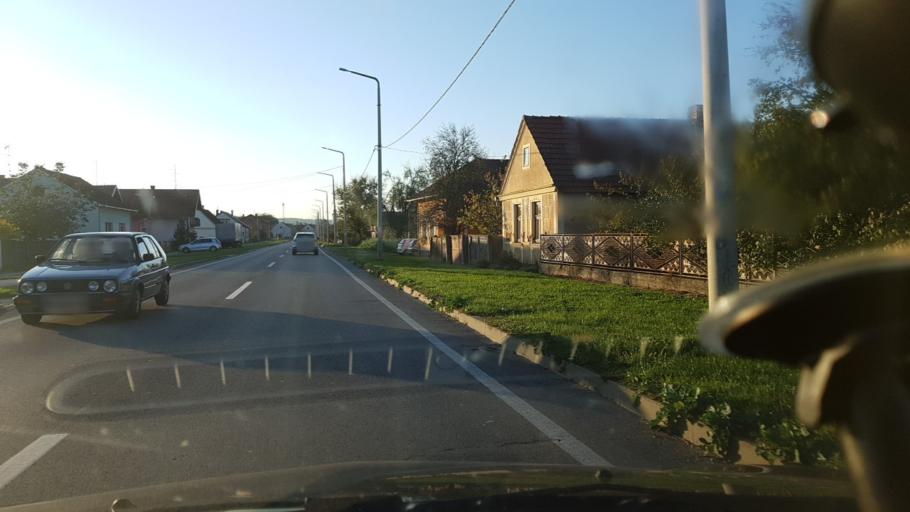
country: HR
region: Koprivnicko-Krizevacka
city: Virje
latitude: 46.0733
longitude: 16.9584
